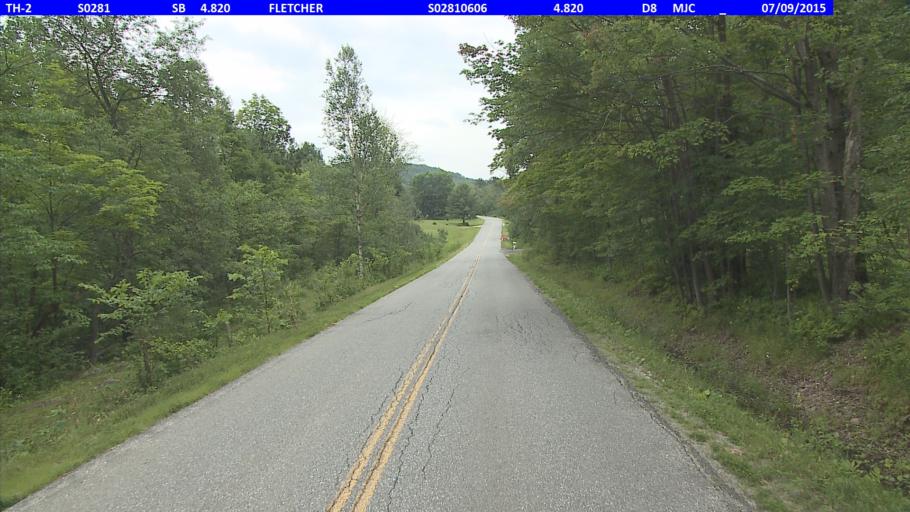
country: US
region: Vermont
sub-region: Franklin County
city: Saint Albans
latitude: 44.7354
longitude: -72.9488
